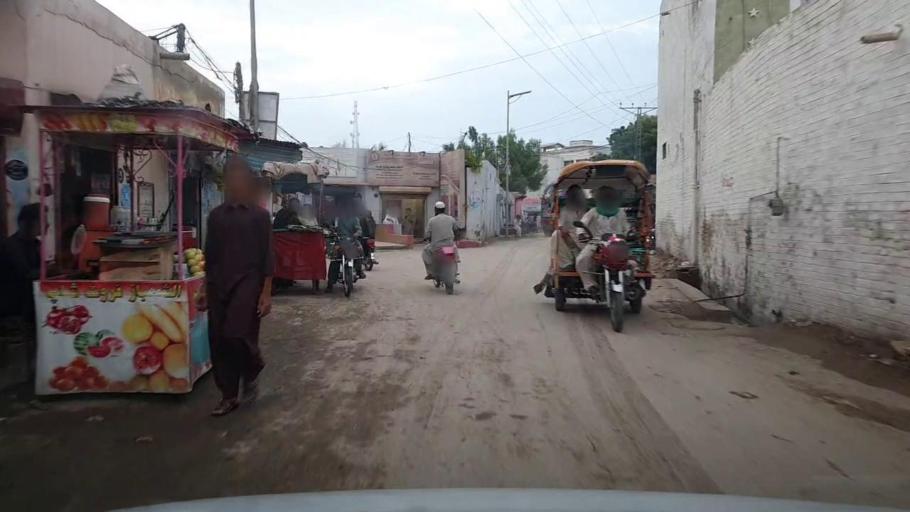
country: PK
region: Sindh
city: Naushahro Firoz
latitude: 26.8371
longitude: 68.1231
